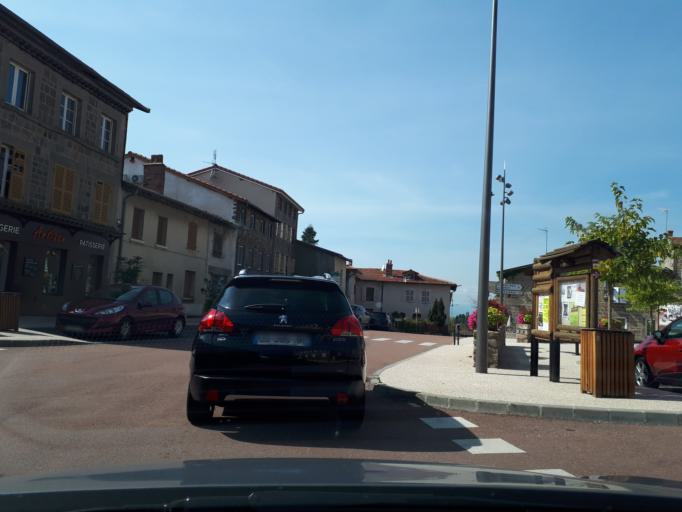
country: FR
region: Rhone-Alpes
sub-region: Departement du Rhone
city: Haute-Rivoire
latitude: 45.7208
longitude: 4.3541
